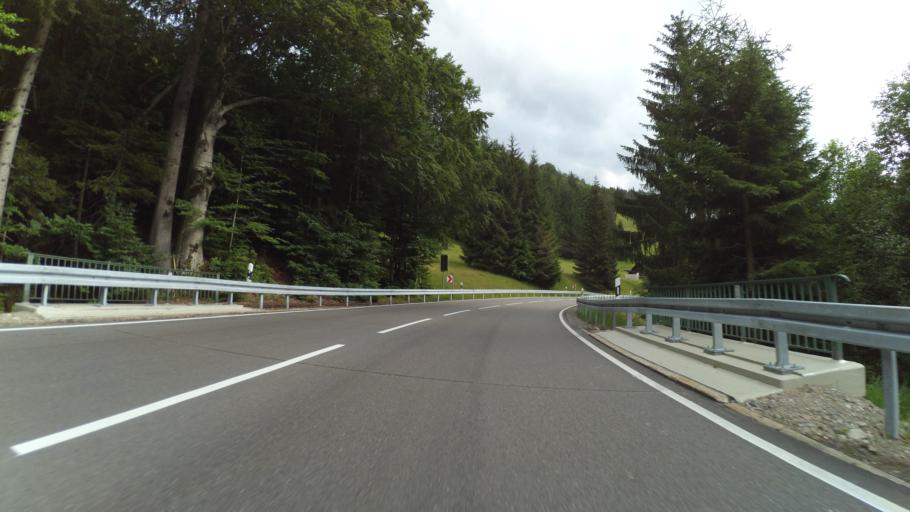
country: DE
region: Baden-Wuerttemberg
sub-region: Freiburg Region
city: Bernau
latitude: 47.8573
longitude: 8.0067
